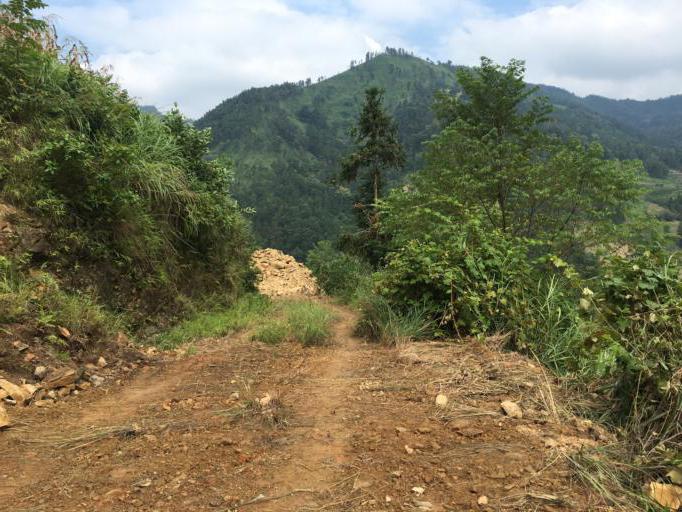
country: CN
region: Guangxi Zhuangzu Zizhiqu
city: Tongle
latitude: 25.3009
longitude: 106.1450
